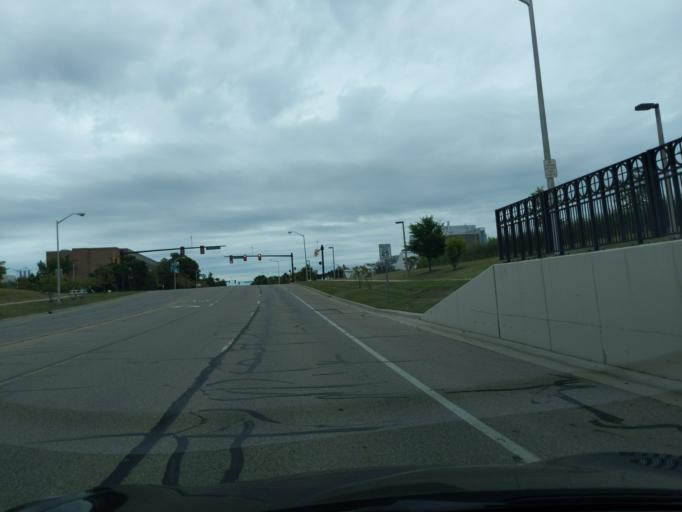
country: US
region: Michigan
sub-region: Ingham County
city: East Lansing
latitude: 42.7204
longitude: -84.4780
